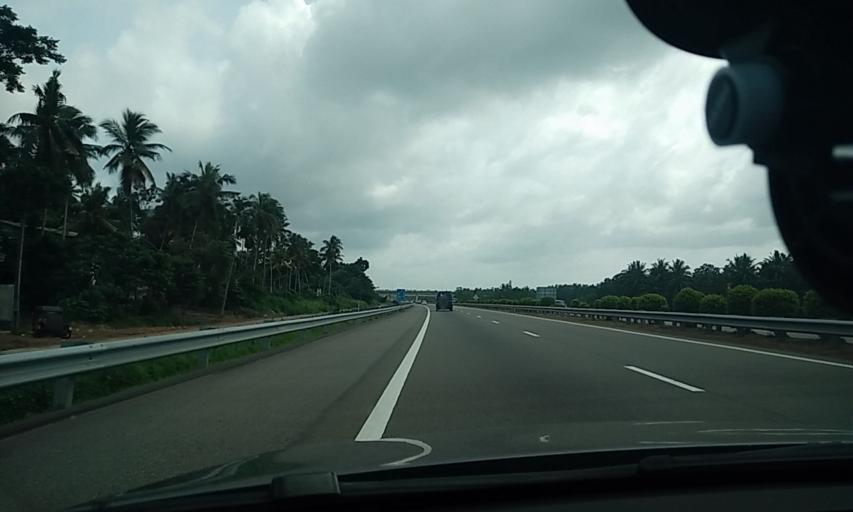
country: LK
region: Western
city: Homagama
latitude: 6.8698
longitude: 79.9783
